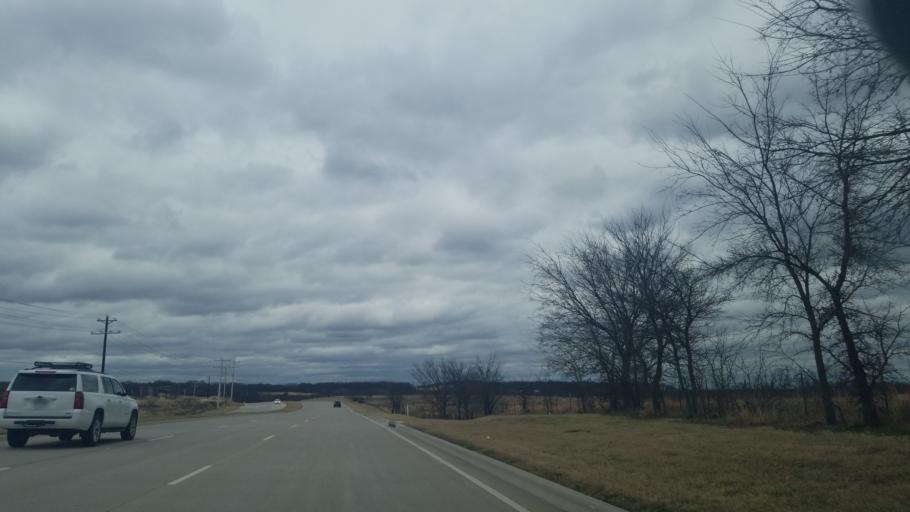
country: US
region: Texas
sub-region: Denton County
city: Trophy Club
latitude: 33.0515
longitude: -97.1907
